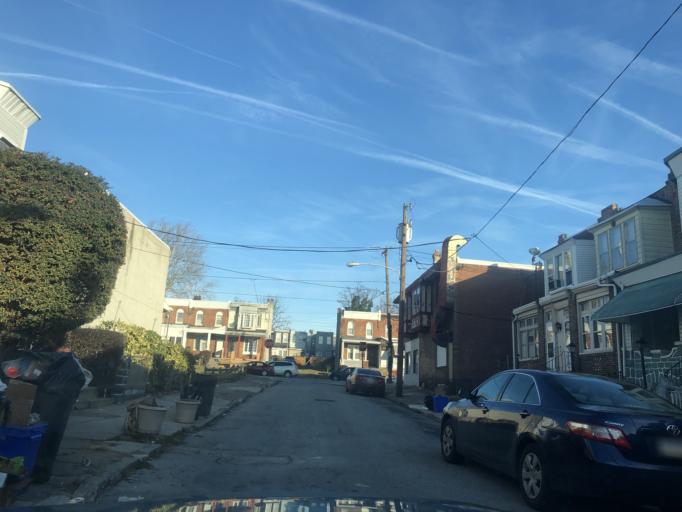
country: US
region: Pennsylvania
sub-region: Delaware County
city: Millbourne
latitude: 39.9701
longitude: -75.2276
